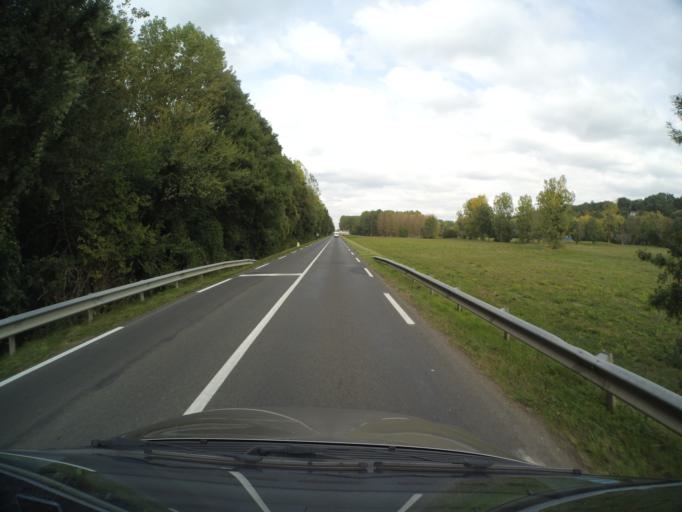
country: FR
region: Centre
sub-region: Departement d'Indre-et-Loire
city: Vernou-sur-Brenne
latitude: 47.4243
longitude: 0.8445
